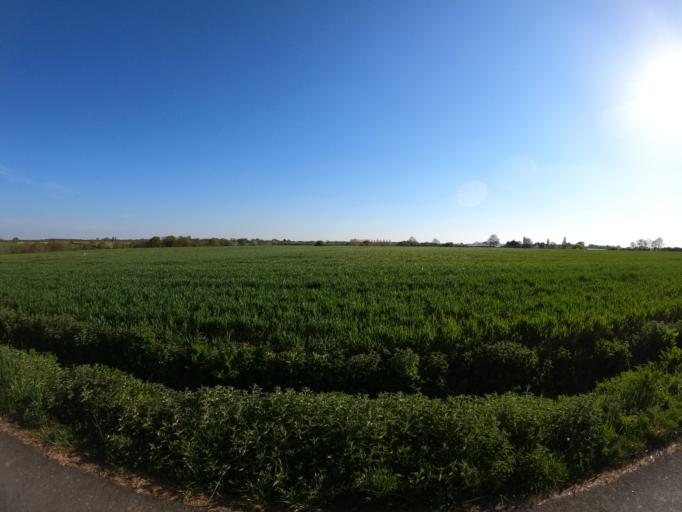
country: FR
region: Pays de la Loire
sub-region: Departement de la Vendee
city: Les Brouzils
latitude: 46.8884
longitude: -1.3430
